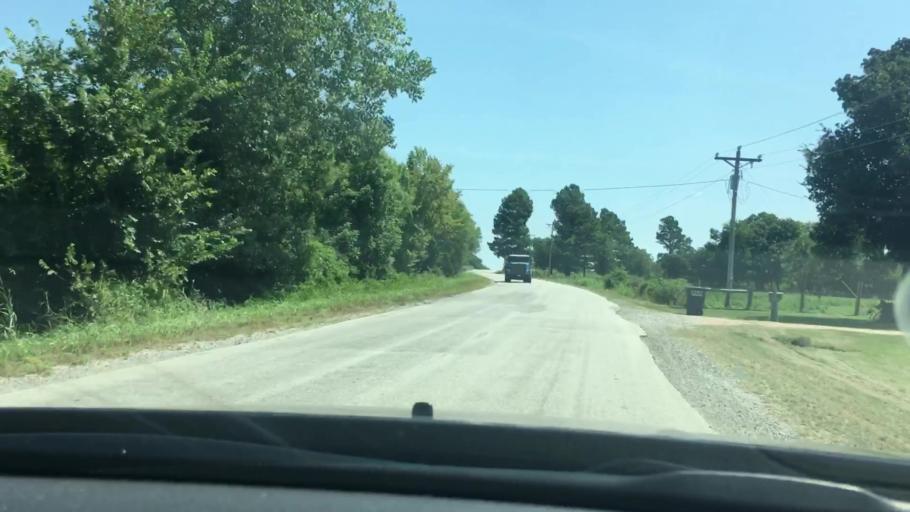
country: US
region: Oklahoma
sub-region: Johnston County
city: Tishomingo
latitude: 34.2587
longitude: -96.4179
